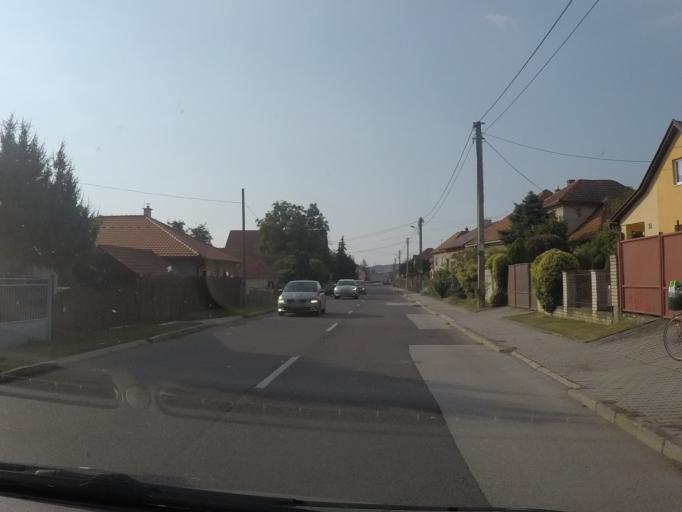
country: SK
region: Nitriansky
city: Tlmace
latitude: 48.3210
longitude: 18.5176
